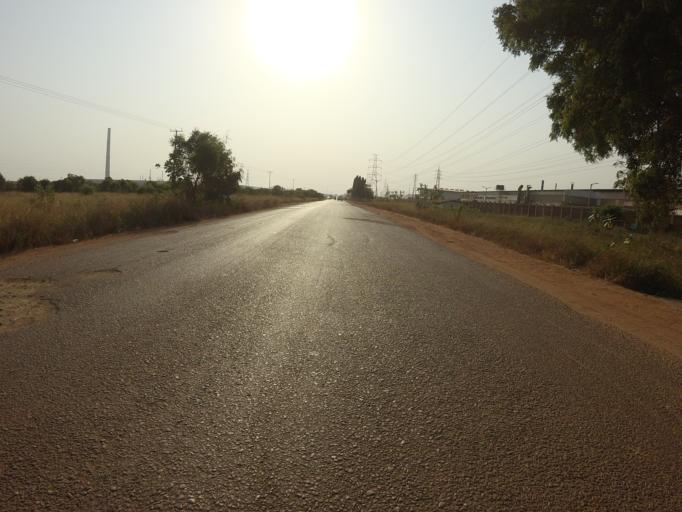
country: GH
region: Greater Accra
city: Tema
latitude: 5.6744
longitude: 0.0283
